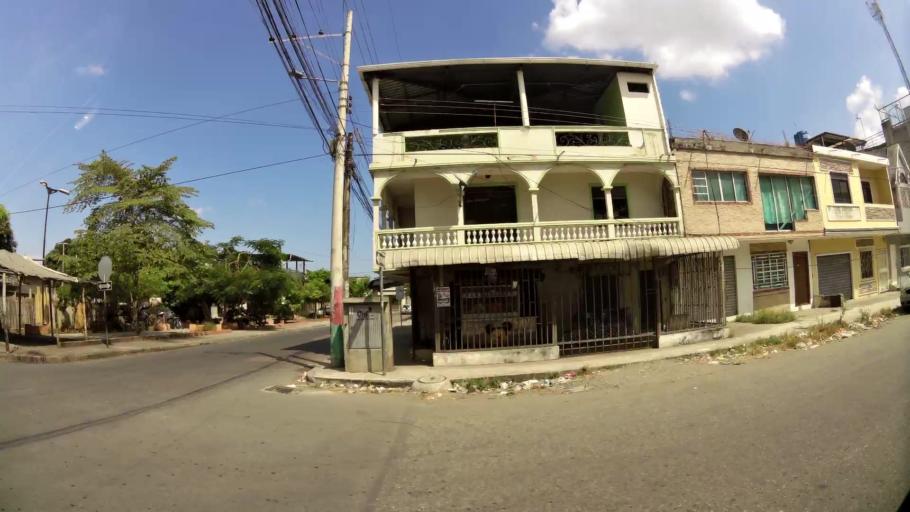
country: EC
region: Guayas
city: Guayaquil
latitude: -2.1338
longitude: -79.9385
